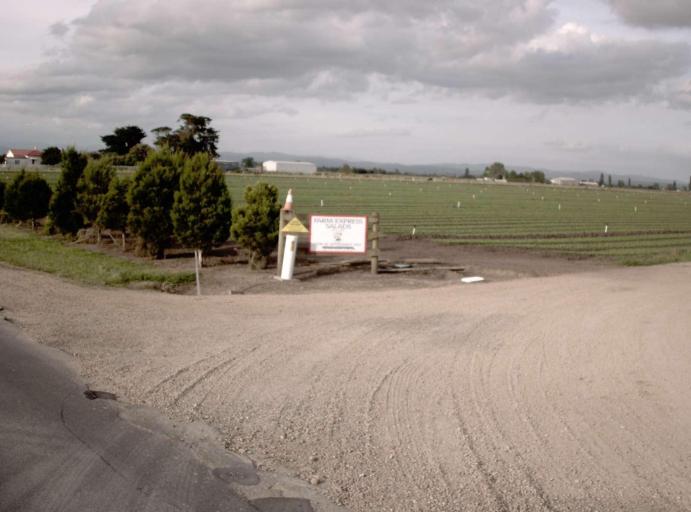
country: AU
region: Victoria
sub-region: Wellington
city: Sale
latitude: -37.9040
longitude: 146.9941
